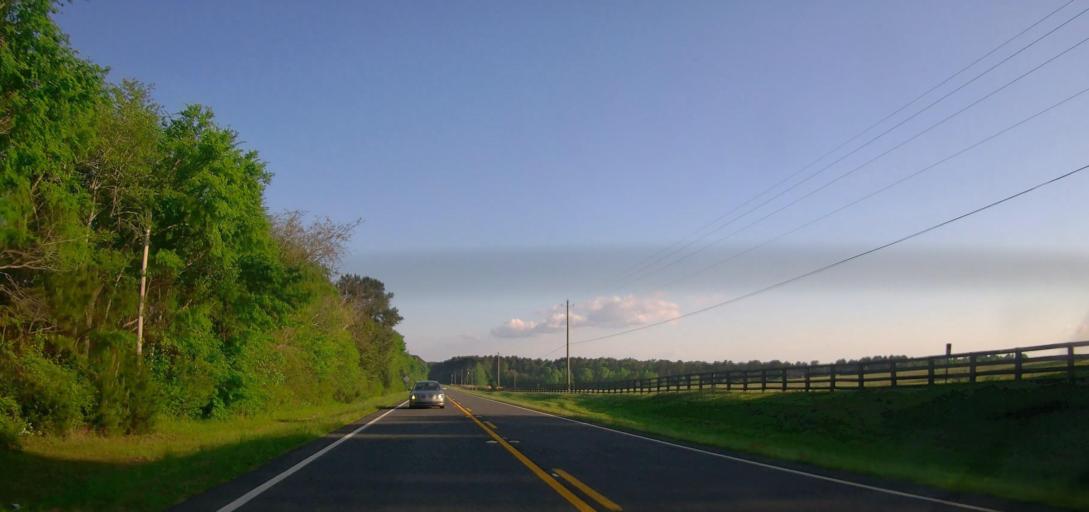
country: US
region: Georgia
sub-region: Jasper County
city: Monticello
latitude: 33.4369
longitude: -83.6199
